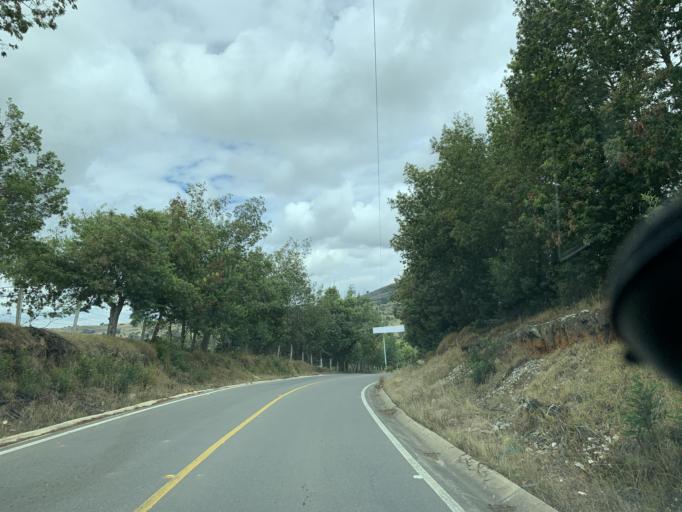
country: CO
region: Boyaca
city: Toca
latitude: 5.5699
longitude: -73.2102
